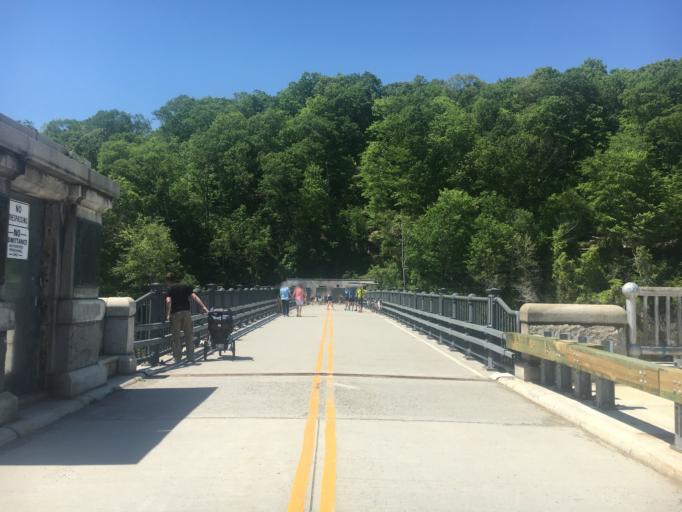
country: US
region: New York
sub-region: Westchester County
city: Croton-on-Hudson
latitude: 41.2275
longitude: -73.8570
